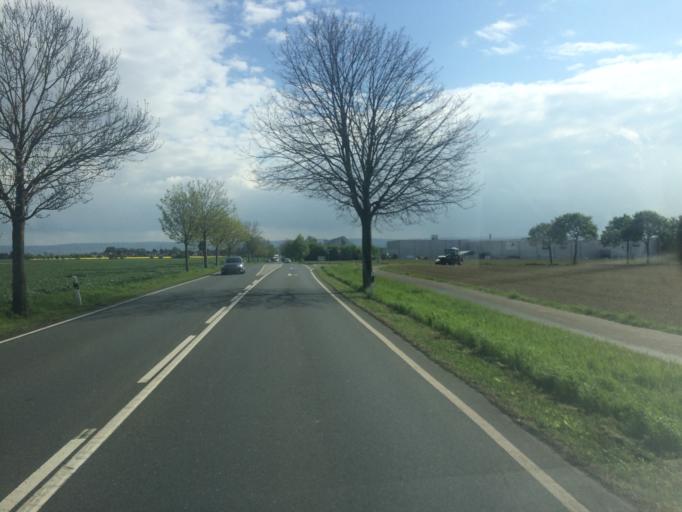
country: DE
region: Lower Saxony
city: Gross Munzel
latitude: 52.3786
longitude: 9.4804
